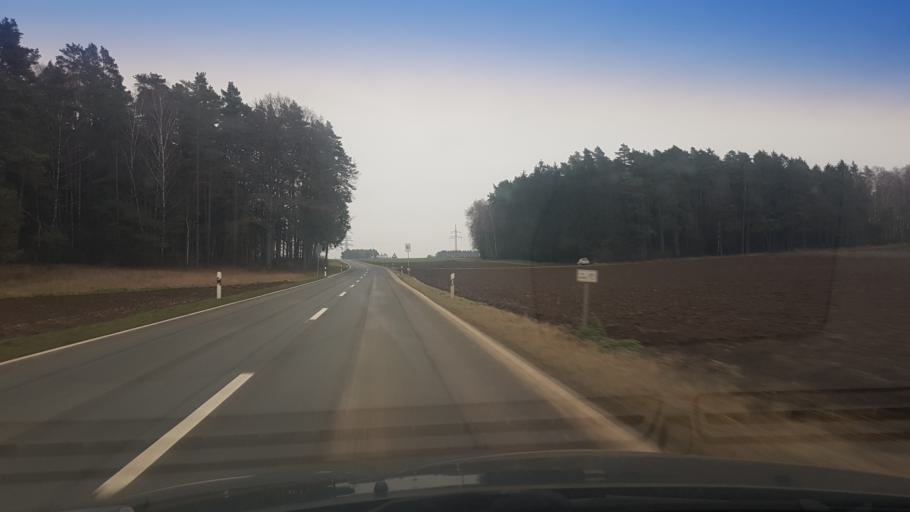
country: DE
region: Bavaria
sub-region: Upper Franconia
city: Wonsees
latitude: 50.0272
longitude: 11.2778
